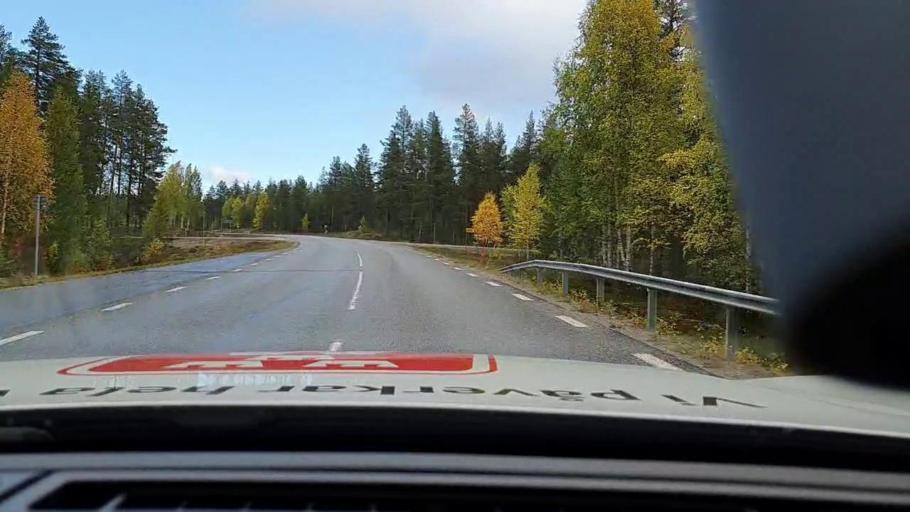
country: SE
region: Vaesterbotten
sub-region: Norsjo Kommun
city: Norsjoe
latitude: 64.9674
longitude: 19.7119
